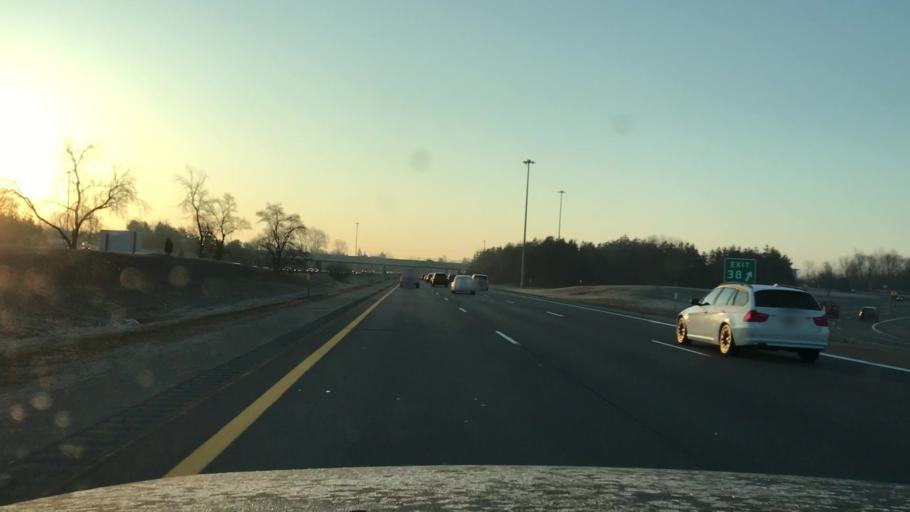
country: US
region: Michigan
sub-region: Kent County
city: East Grand Rapids
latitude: 42.9738
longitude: -85.5953
